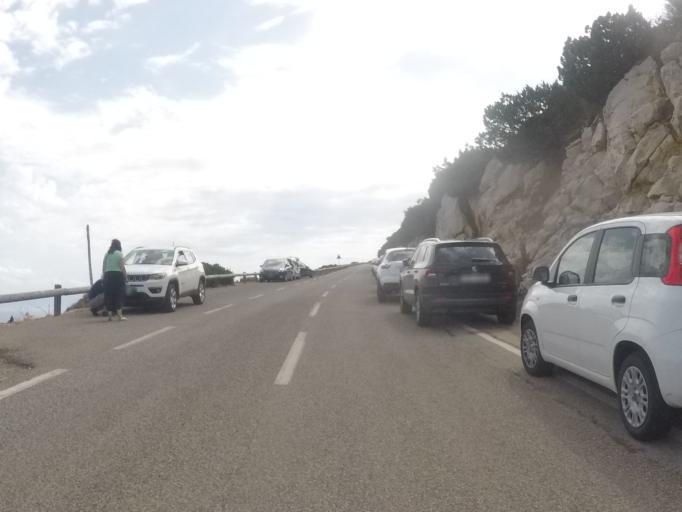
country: IT
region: Sardinia
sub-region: Provincia di Sassari
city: Alghero
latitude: 40.5696
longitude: 8.1630
